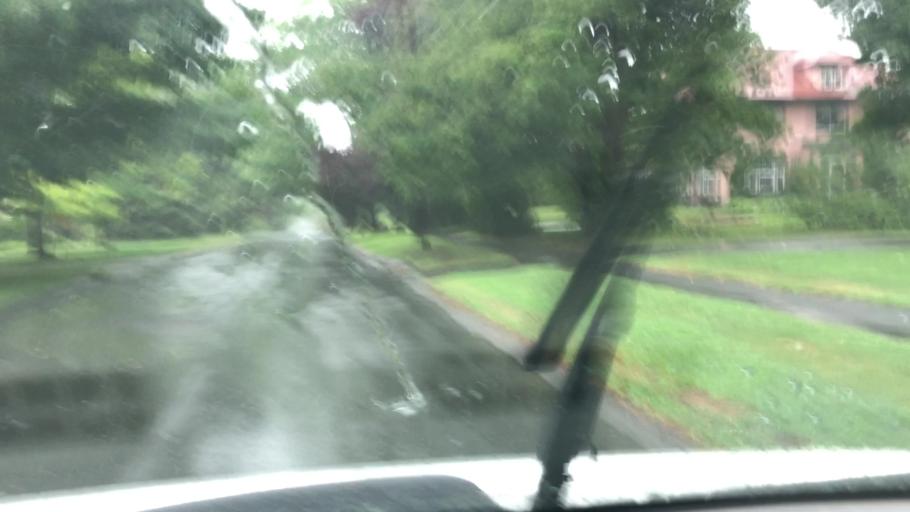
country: US
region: Massachusetts
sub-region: Berkshire County
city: Pittsfield
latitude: 42.4400
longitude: -73.2446
